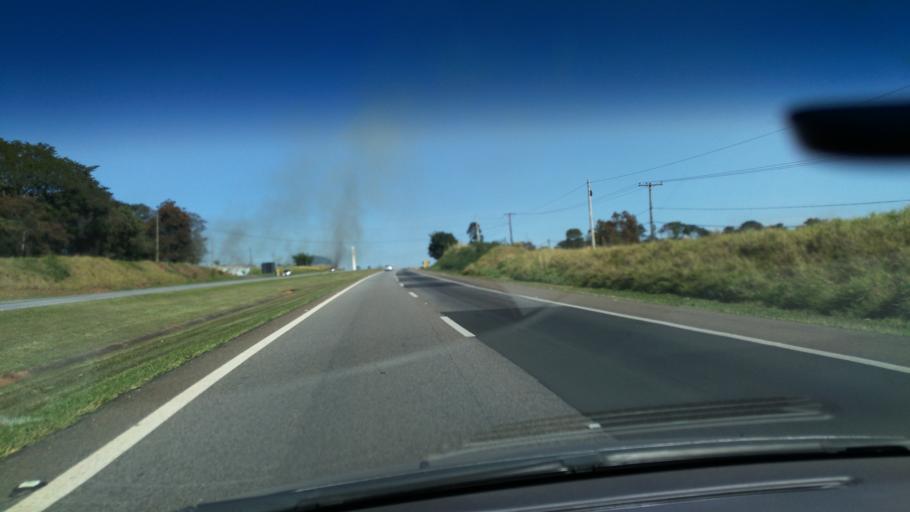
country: BR
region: Sao Paulo
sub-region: Mogi-Mirim
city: Mogi Mirim
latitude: -22.5004
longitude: -46.9846
